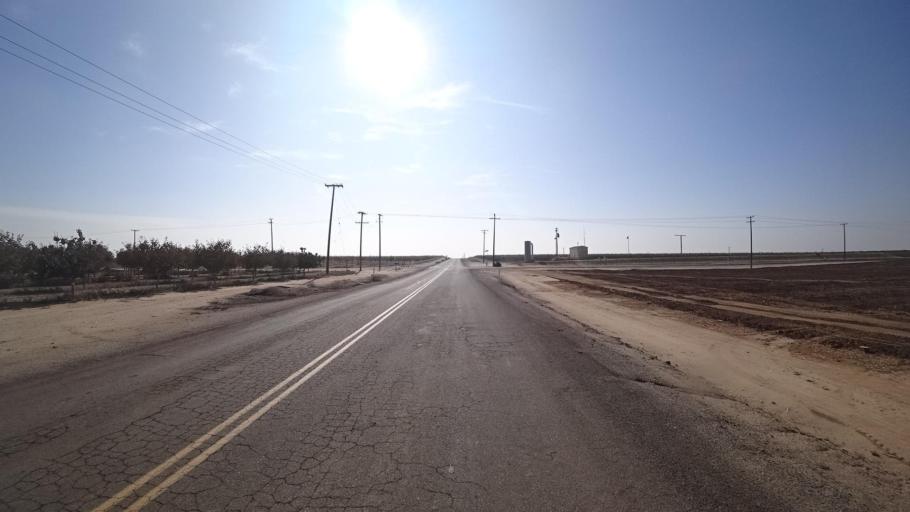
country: US
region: California
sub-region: Kern County
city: McFarland
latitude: 35.6319
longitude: -119.1689
